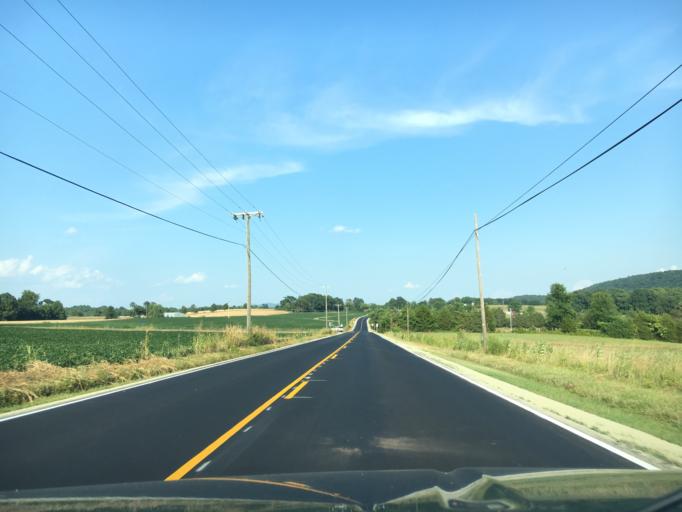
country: US
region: Virginia
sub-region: Franklin County
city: Union Hall
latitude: 36.9863
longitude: -79.7437
